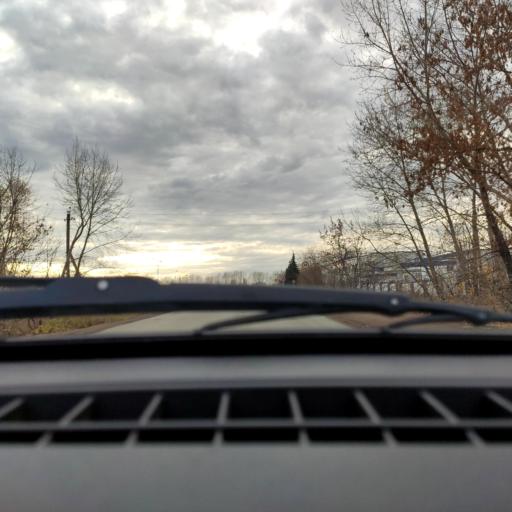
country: RU
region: Bashkortostan
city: Ufa
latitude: 54.8622
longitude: 56.1161
